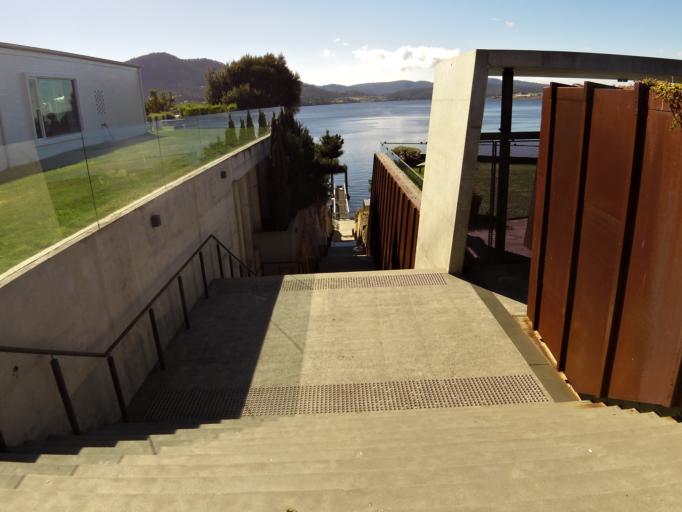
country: AU
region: Tasmania
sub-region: Glenorchy
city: Berriedale
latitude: -42.8126
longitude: 147.2616
